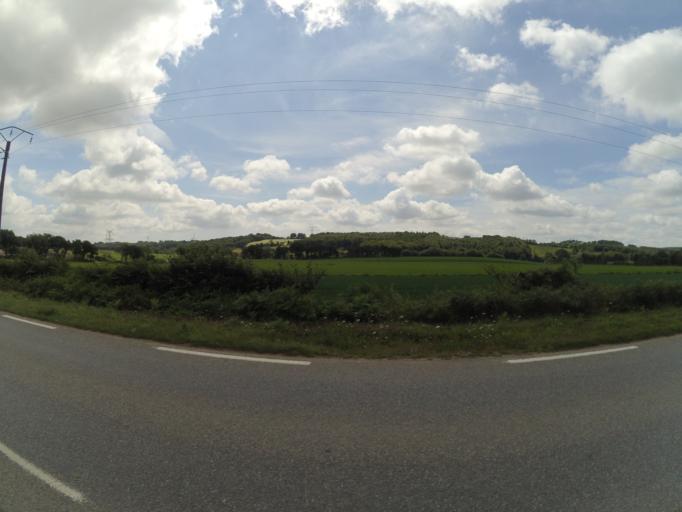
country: FR
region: Brittany
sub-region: Departement du Finistere
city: Elliant
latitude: 47.9682
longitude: -3.8790
